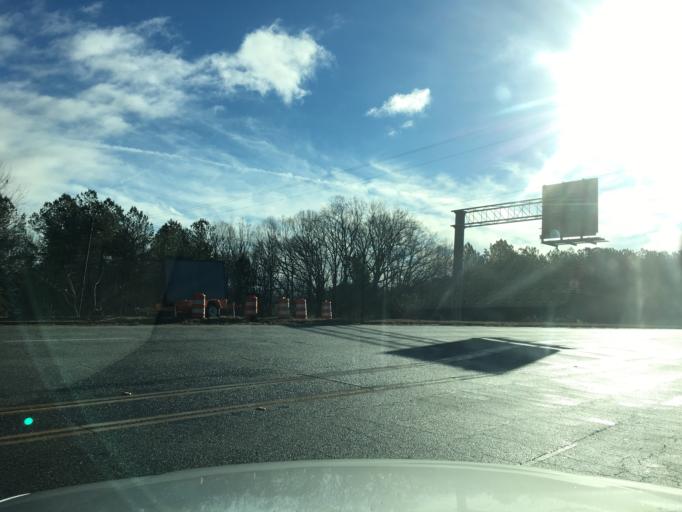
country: US
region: South Carolina
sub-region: Spartanburg County
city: Mayo
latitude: 35.0235
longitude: -81.8744
